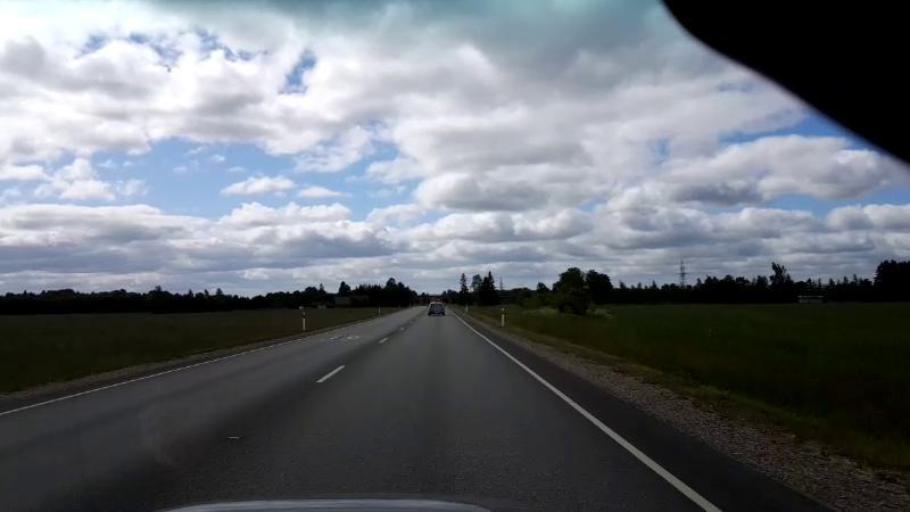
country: EE
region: Paernumaa
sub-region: Halinga vald
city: Parnu-Jaagupi
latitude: 58.5845
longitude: 24.5123
